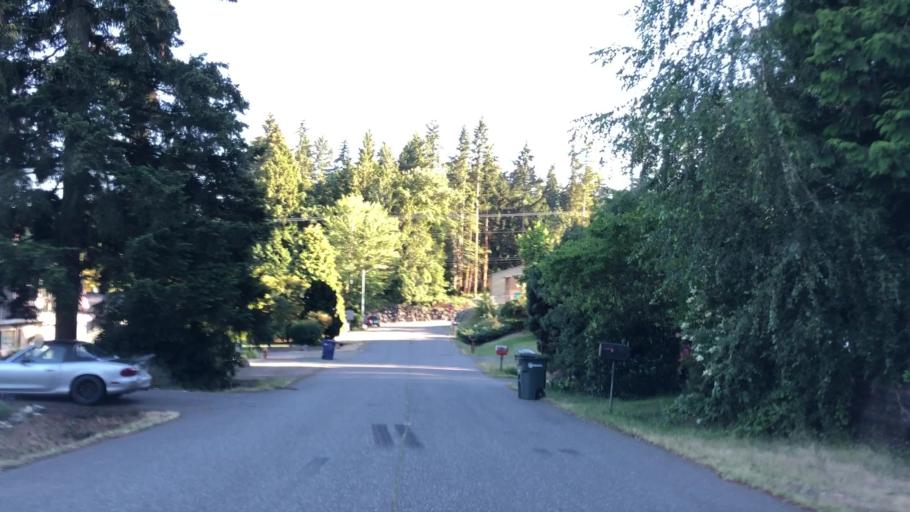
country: US
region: Washington
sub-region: King County
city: Bothell
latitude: 47.7926
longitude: -122.2276
